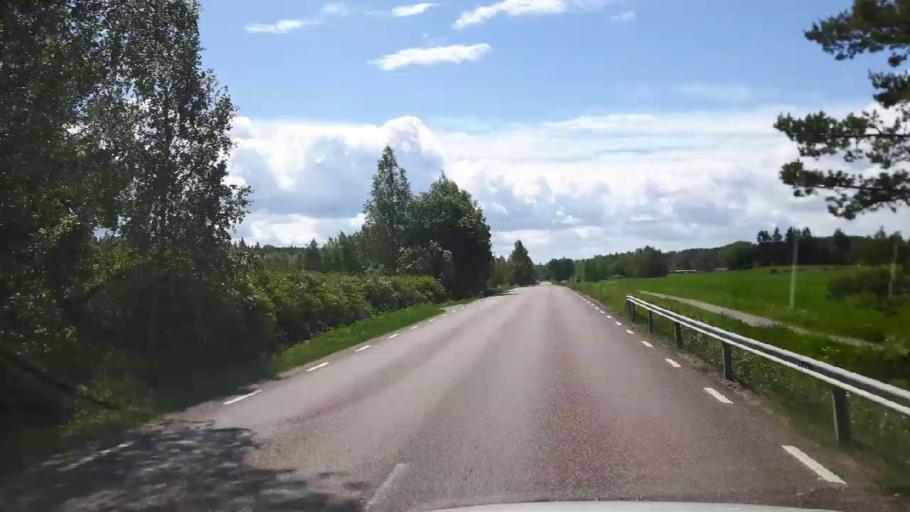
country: SE
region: Dalarna
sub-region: Faluns Kommun
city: Falun
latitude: 60.6081
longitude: 15.7712
